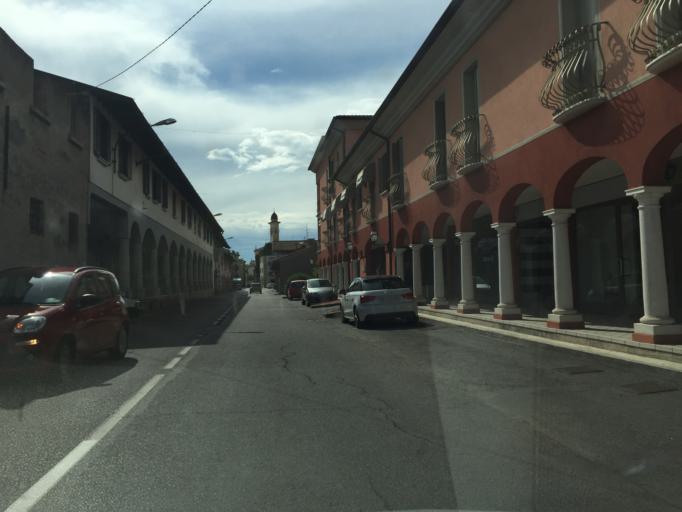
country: IT
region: Lombardy
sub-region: Provincia di Brescia
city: Flero
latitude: 45.4828
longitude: 10.1787
